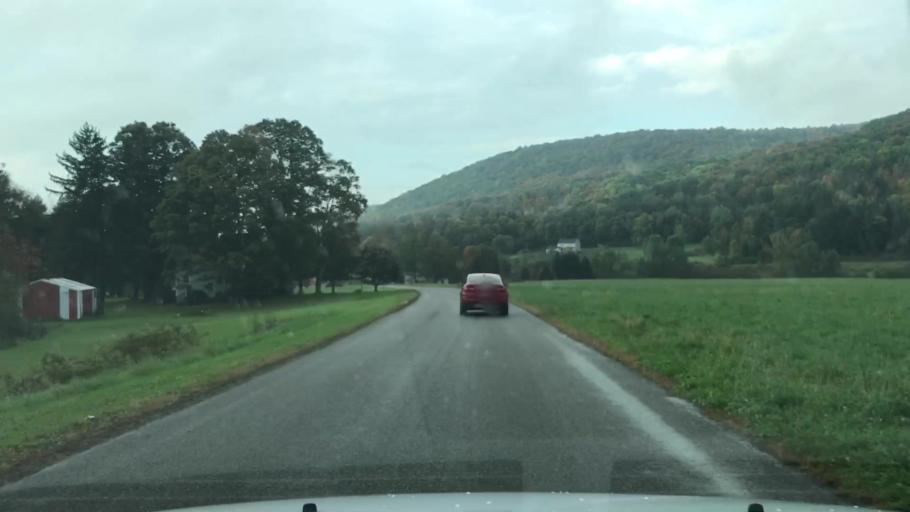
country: US
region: New York
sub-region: Cattaraugus County
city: Little Valley
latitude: 42.3001
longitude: -78.7164
